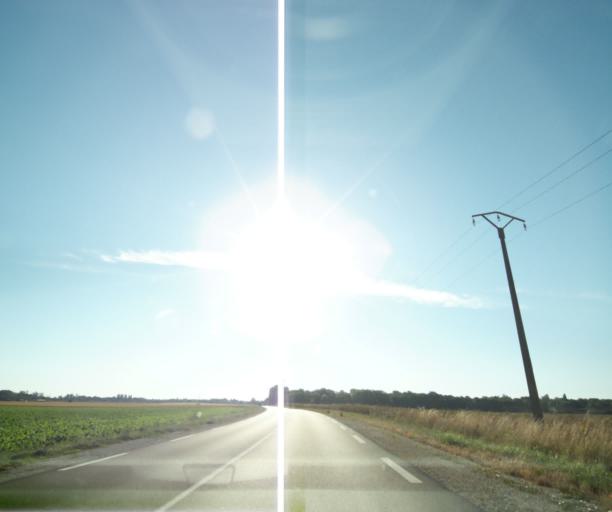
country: FR
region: Ile-de-France
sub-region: Departement de Seine-et-Marne
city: Saint-Germain-Laval
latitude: 48.3827
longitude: 3.0074
